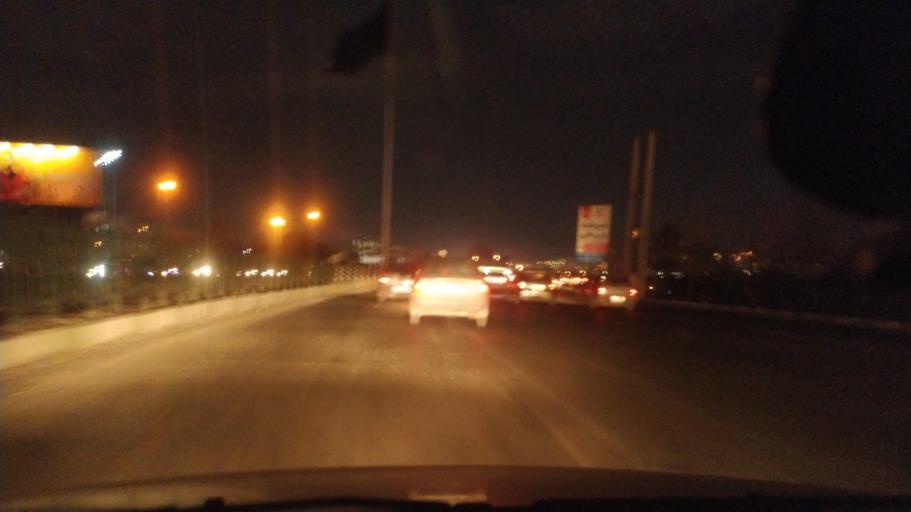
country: IR
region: Alborz
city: Karaj
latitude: 35.7892
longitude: 51.0038
